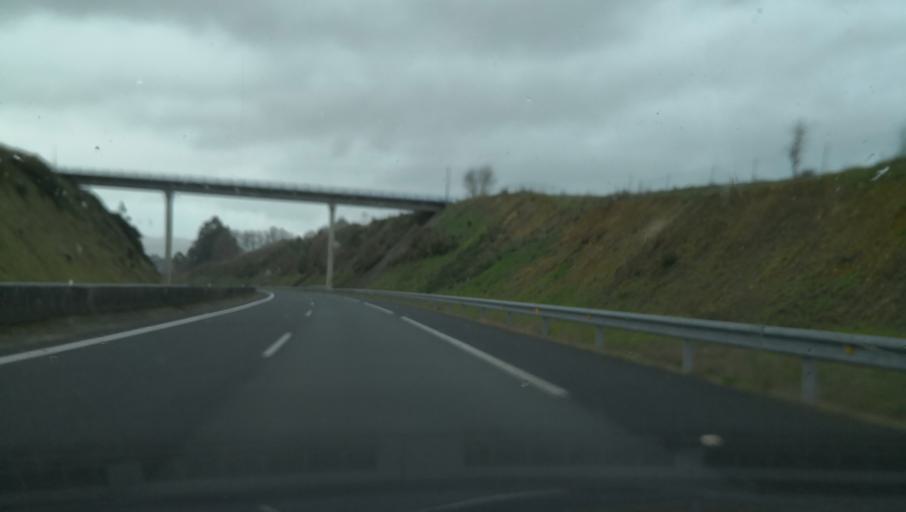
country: ES
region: Galicia
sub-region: Provincia de Pontevedra
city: Lalin
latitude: 42.6866
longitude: -8.1670
